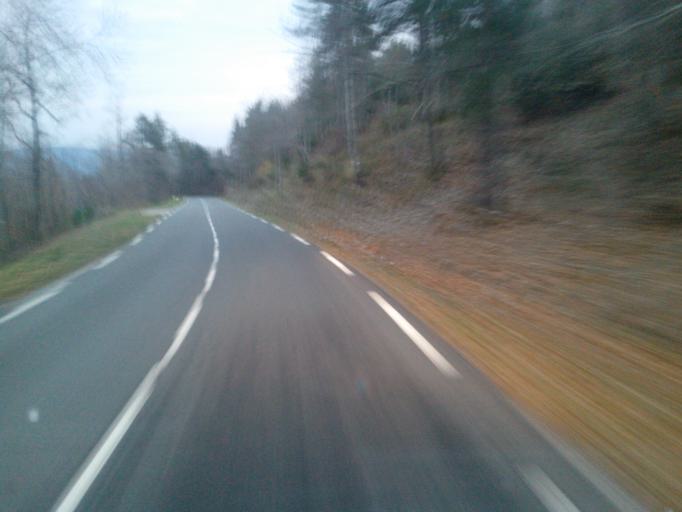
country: FR
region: Languedoc-Roussillon
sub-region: Departement du Gard
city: Valleraugue
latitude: 44.1570
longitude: 3.7413
